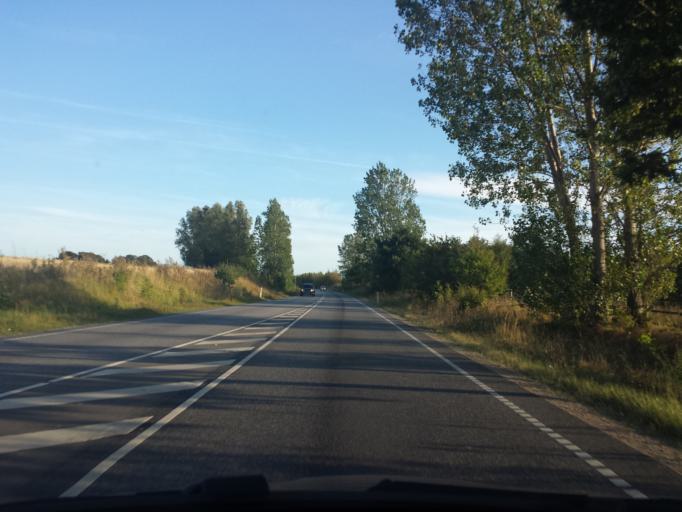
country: DK
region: Zealand
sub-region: Roskilde Kommune
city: Jyllinge
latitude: 55.8030
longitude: 12.1025
